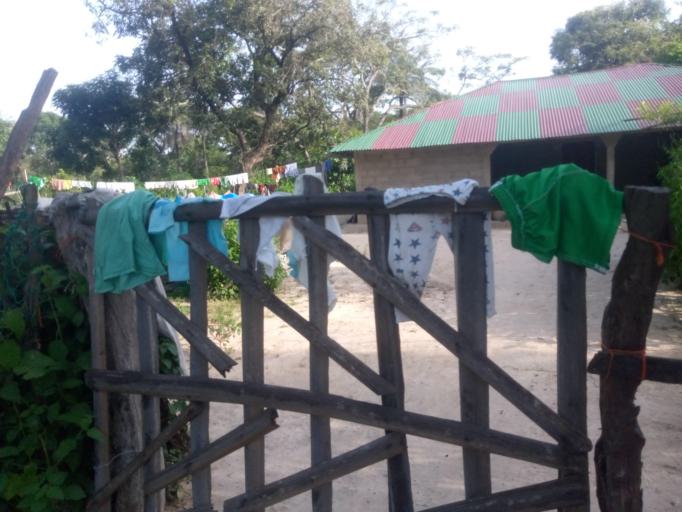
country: GM
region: Western
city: Gunjur
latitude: 13.0347
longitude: -16.7251
